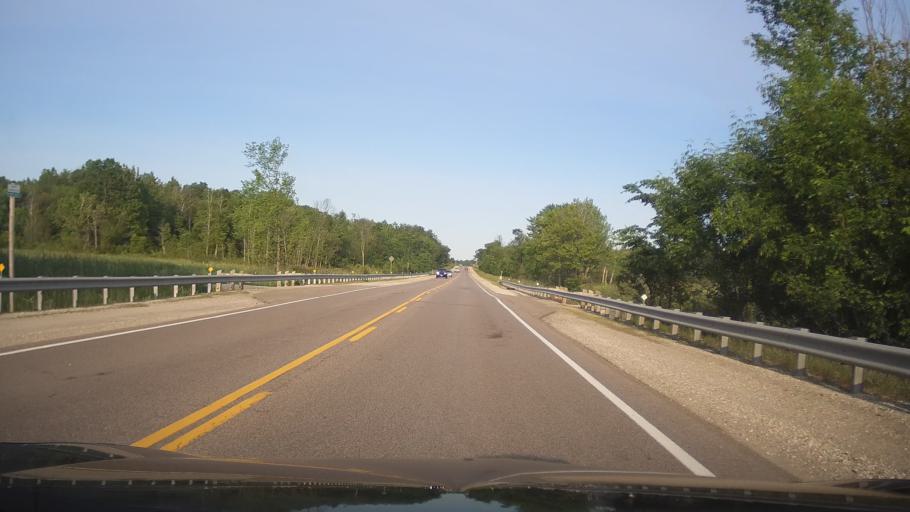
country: CA
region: Ontario
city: Perth
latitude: 44.8669
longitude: -76.3997
